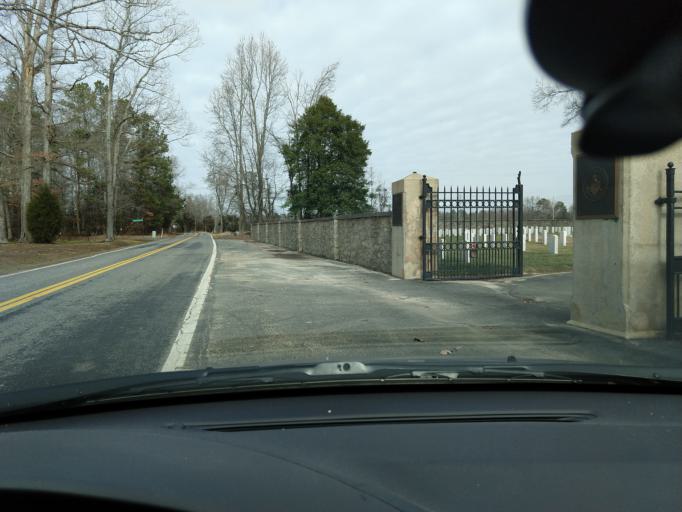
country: US
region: Virginia
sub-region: Henrico County
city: Fort Lee
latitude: 37.4361
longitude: -77.2352
